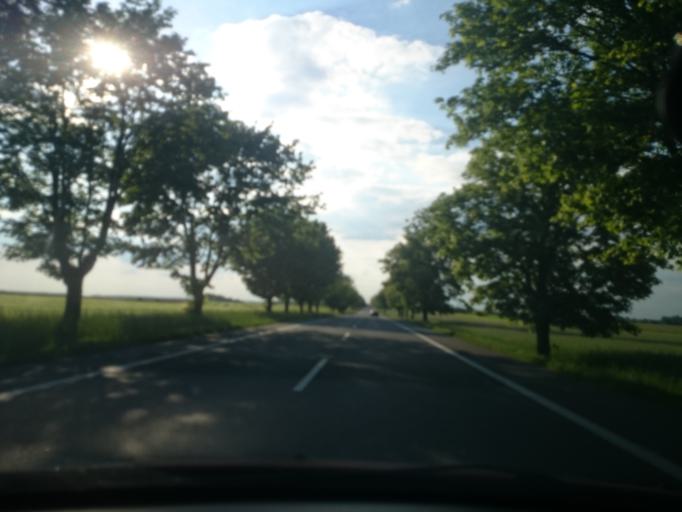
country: PL
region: Opole Voivodeship
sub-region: Powiat strzelecki
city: Izbicko
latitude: 50.5661
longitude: 18.1680
